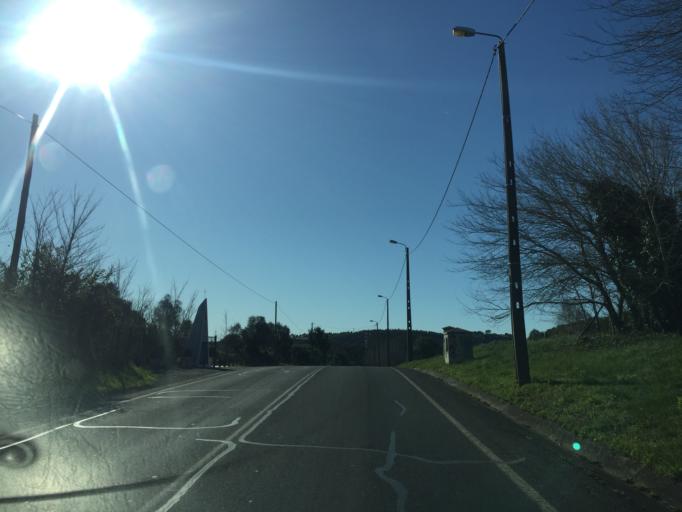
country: PT
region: Lisbon
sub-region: Sintra
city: Almargem
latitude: 38.8194
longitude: -9.2914
